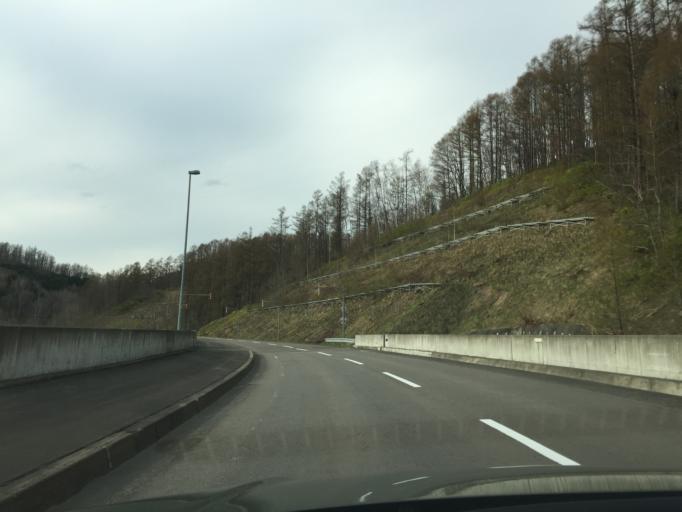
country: JP
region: Hokkaido
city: Utashinai
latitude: 43.5208
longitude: 142.0244
